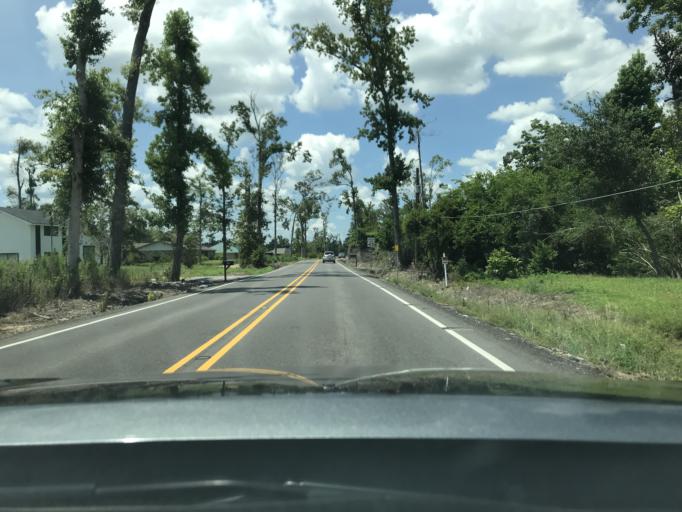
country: US
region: Louisiana
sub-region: Calcasieu Parish
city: Moss Bluff
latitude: 30.3088
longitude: -93.1822
